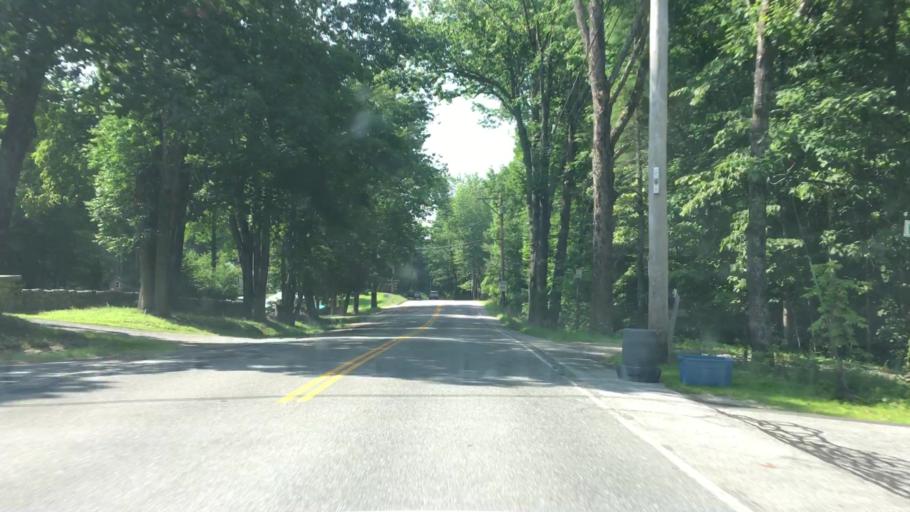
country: US
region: Maine
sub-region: Cumberland County
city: Raymond
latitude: 43.9112
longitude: -70.4396
